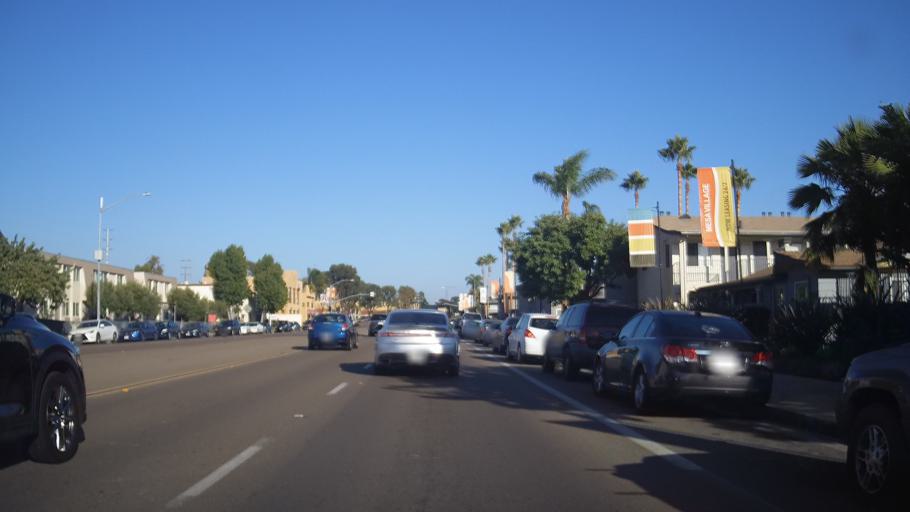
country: US
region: California
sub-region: San Diego County
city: La Jolla
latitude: 32.8343
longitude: -117.1778
